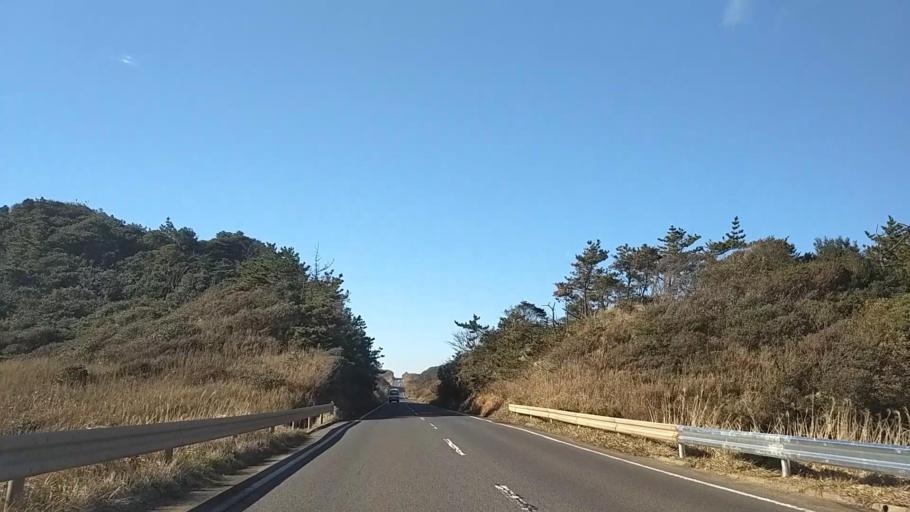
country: JP
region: Chiba
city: Hasaki
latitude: 35.7138
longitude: 140.8138
